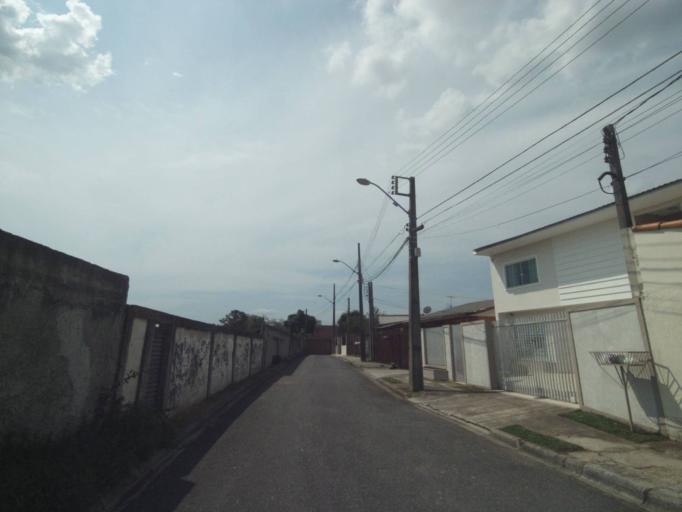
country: BR
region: Parana
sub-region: Pinhais
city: Pinhais
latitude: -25.4033
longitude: -49.2119
